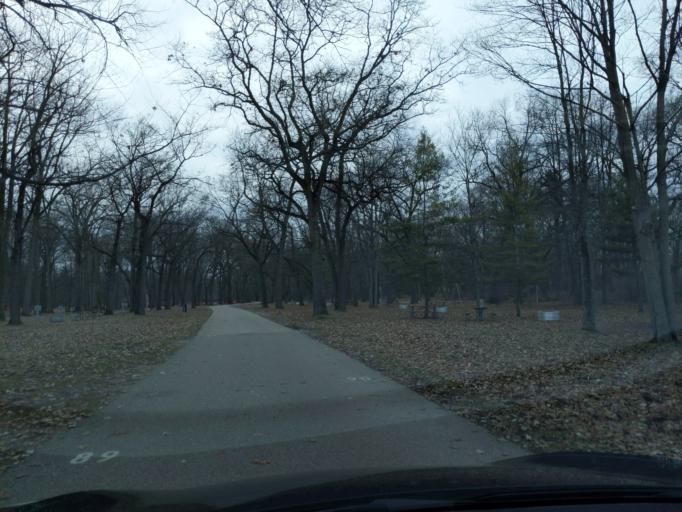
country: US
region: Michigan
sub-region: Bay County
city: Bay City
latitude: 43.6643
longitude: -83.9006
